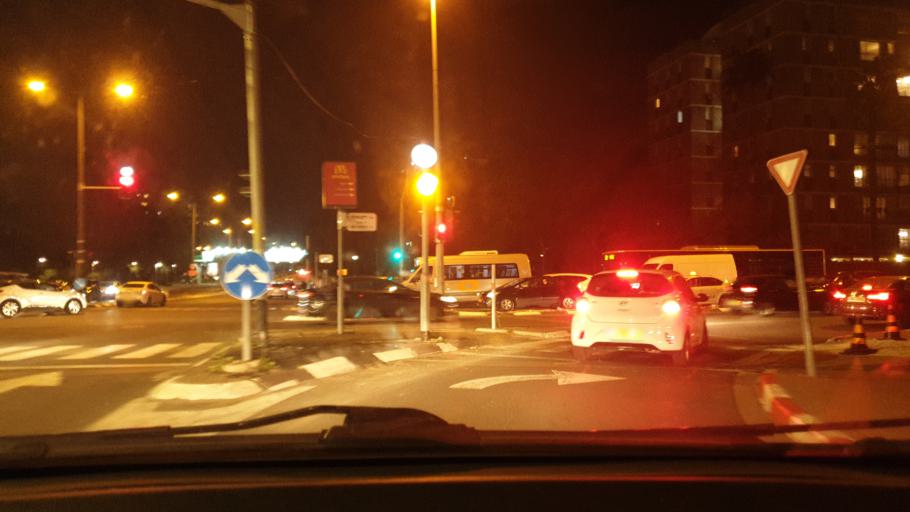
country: IL
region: Tel Aviv
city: Ramat Gan
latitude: 32.1215
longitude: 34.8025
